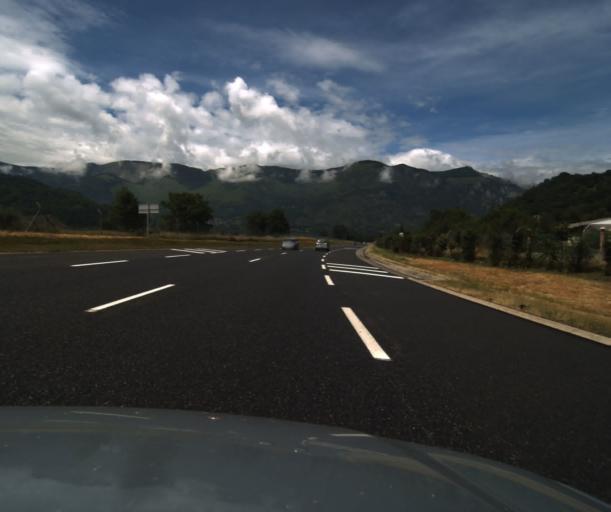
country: FR
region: Midi-Pyrenees
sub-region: Departement des Hautes-Pyrenees
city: Argeles-Gazost
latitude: 43.0070
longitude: -0.0851
